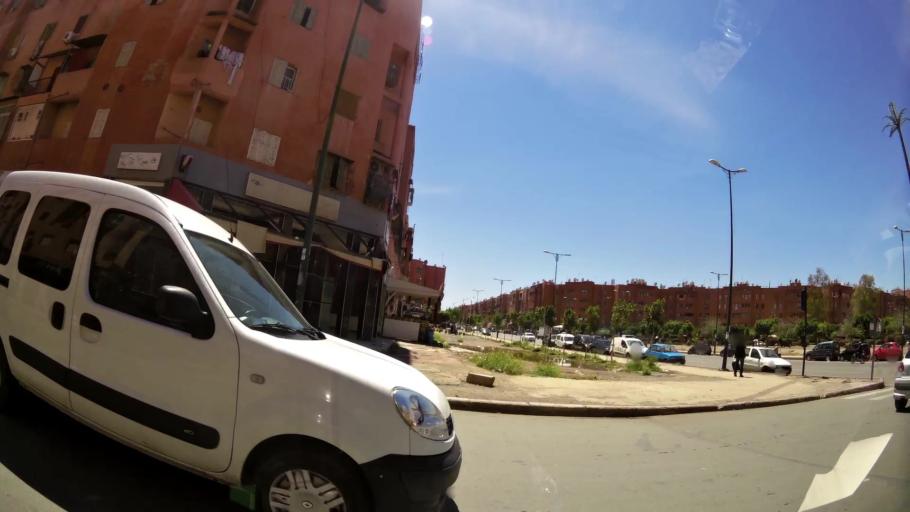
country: MA
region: Marrakech-Tensift-Al Haouz
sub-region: Marrakech
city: Marrakesh
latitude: 31.6349
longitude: -8.0577
